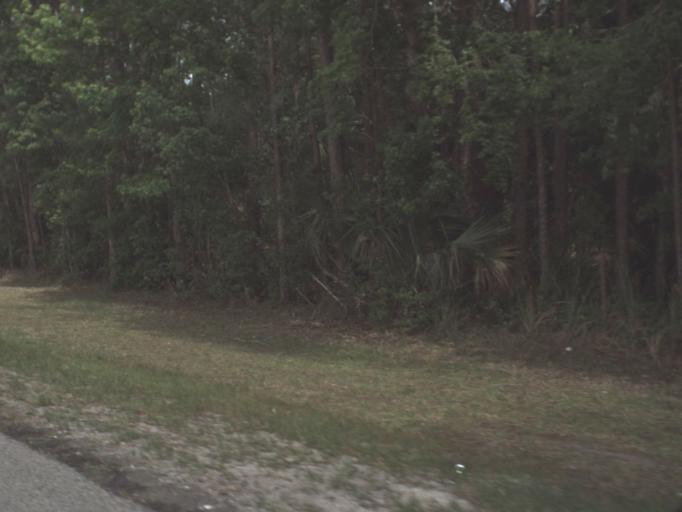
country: US
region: Florida
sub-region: Flagler County
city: Bunnell
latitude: 29.3165
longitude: -81.3119
